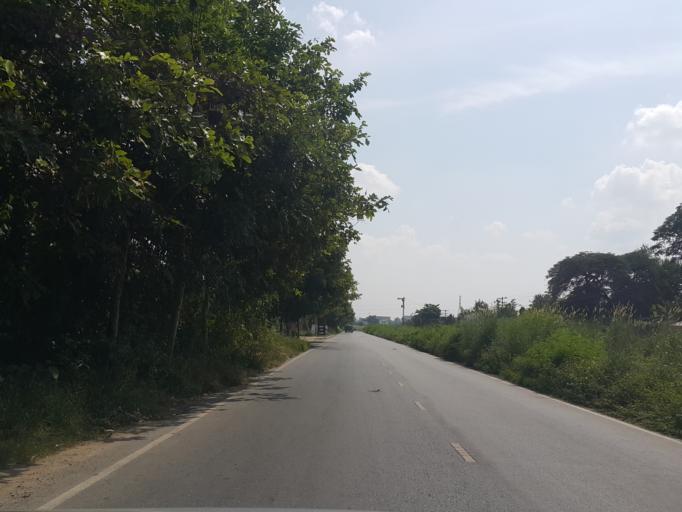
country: TH
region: Chiang Mai
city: Chiang Mai
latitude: 18.7729
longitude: 99.0173
